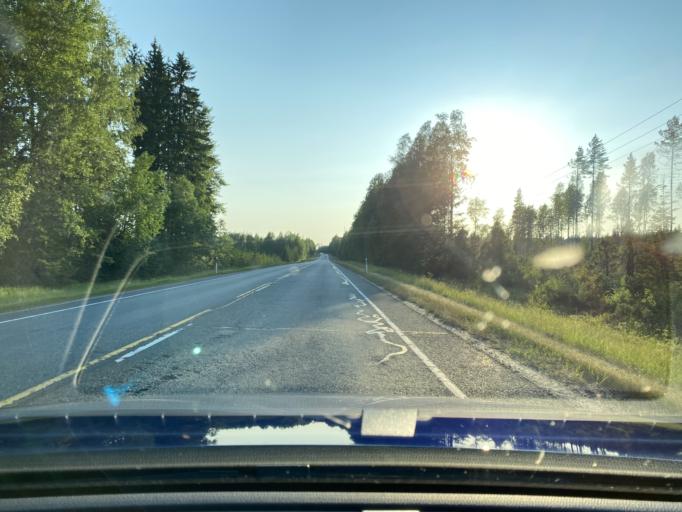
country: FI
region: Haeme
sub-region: Forssa
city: Tammela
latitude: 60.8277
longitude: 23.8952
